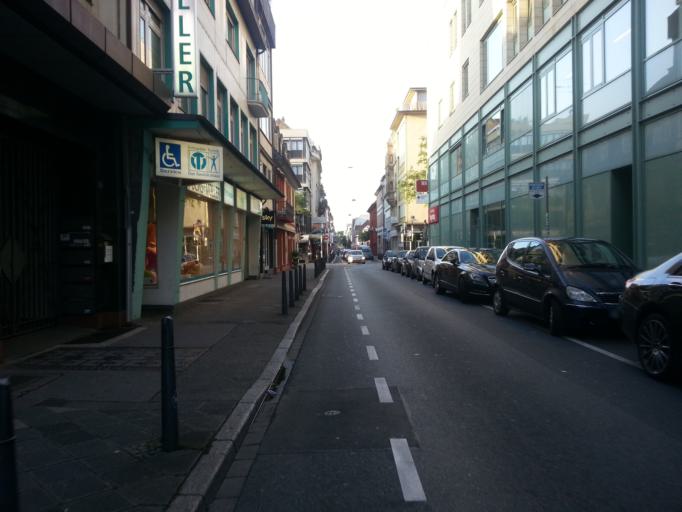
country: DE
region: Baden-Wuerttemberg
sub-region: Karlsruhe Region
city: Mannheim
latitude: 49.4886
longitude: 8.4658
